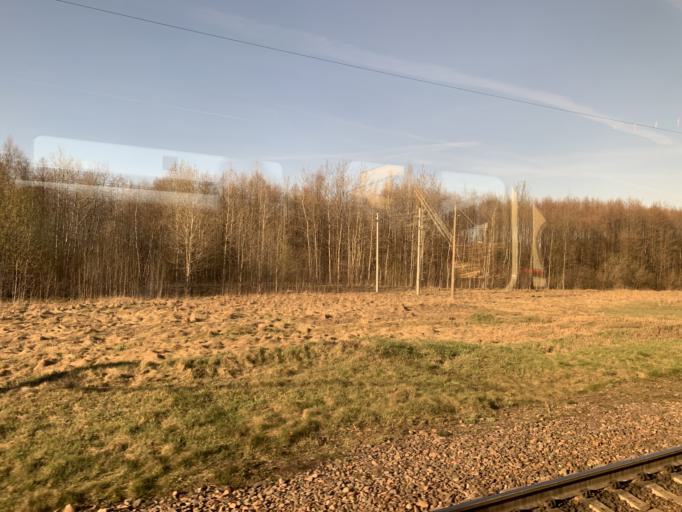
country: BY
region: Minsk
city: Nasilava
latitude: 54.3146
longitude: 26.7994
